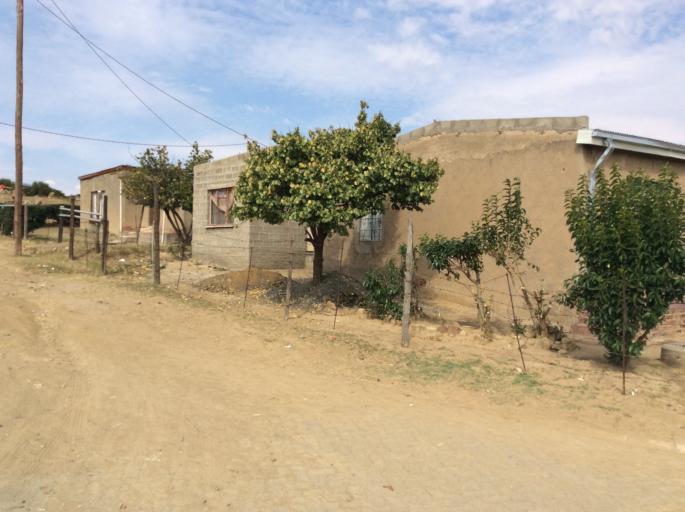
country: ZA
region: Orange Free State
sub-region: Xhariep District Municipality
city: Dewetsdorp
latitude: -29.5877
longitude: 26.6810
